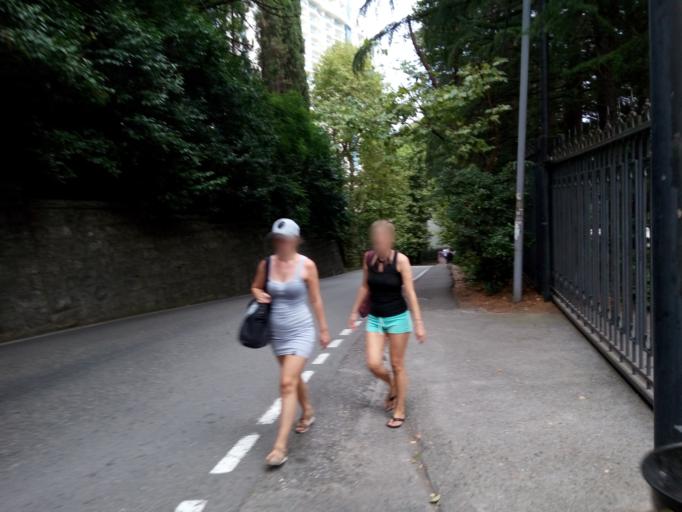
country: RU
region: Krasnodarskiy
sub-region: Sochi City
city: Sochi
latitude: 43.5636
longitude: 39.7611
